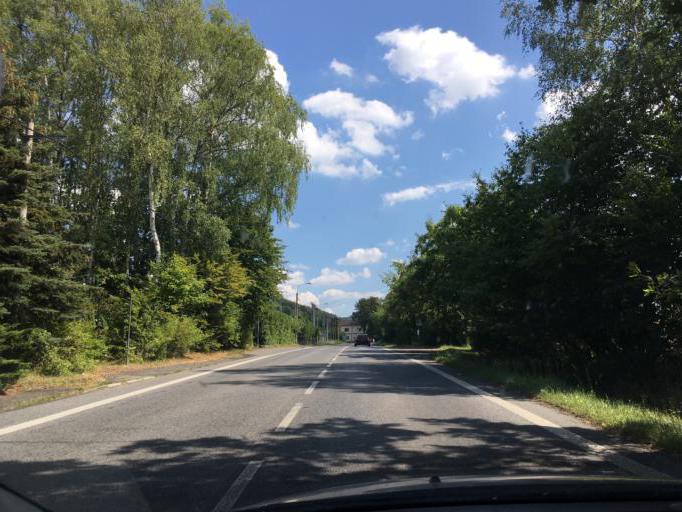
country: CZ
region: Ustecky
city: Ceska Kamenice
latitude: 50.7969
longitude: 14.4454
